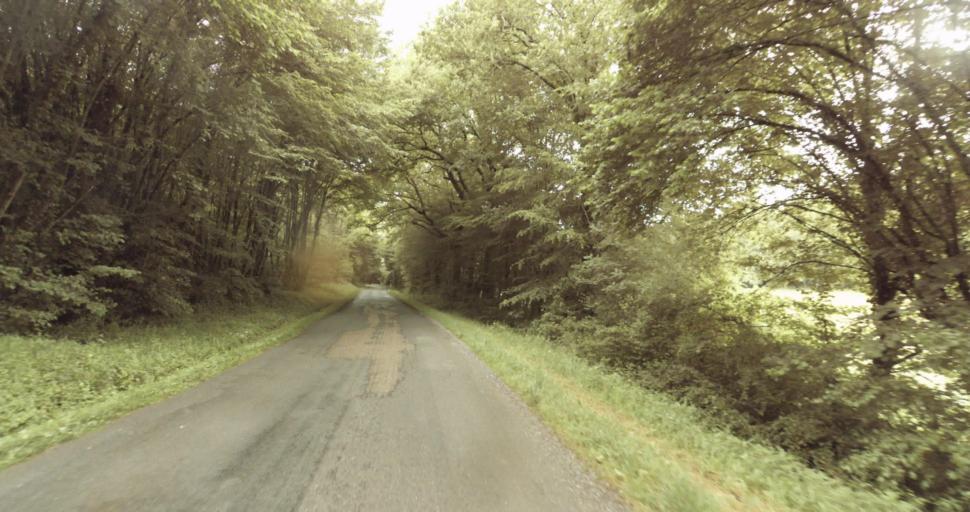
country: FR
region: Aquitaine
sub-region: Departement de la Dordogne
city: Belves
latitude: 44.7531
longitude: 0.9421
